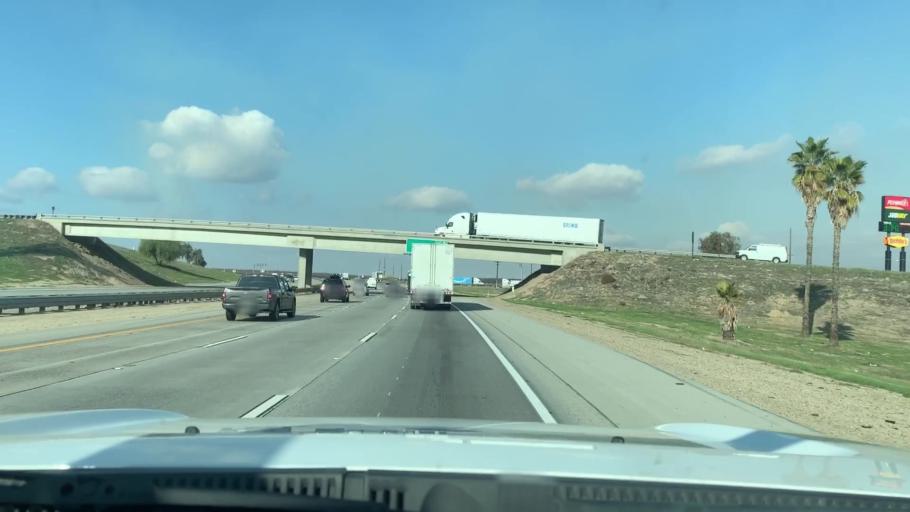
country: US
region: California
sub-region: Kern County
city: Shafter
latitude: 35.5293
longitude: -119.1889
